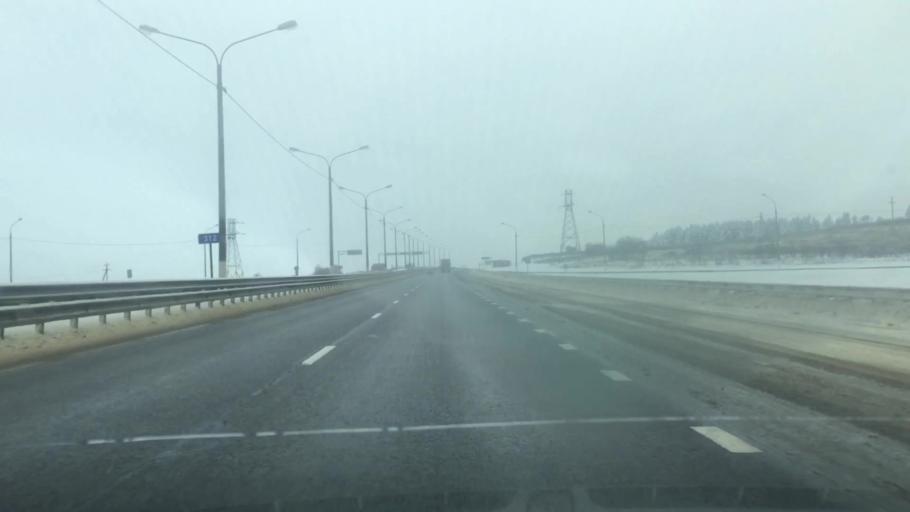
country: RU
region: Tula
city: Yefremov
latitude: 53.1619
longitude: 38.2488
